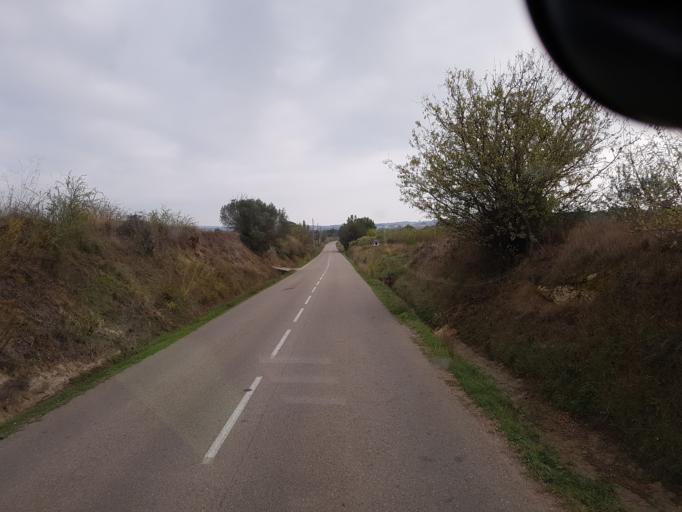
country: FR
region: Languedoc-Roussillon
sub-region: Departement de l'Herault
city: Meze
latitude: 43.4450
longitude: 3.5828
